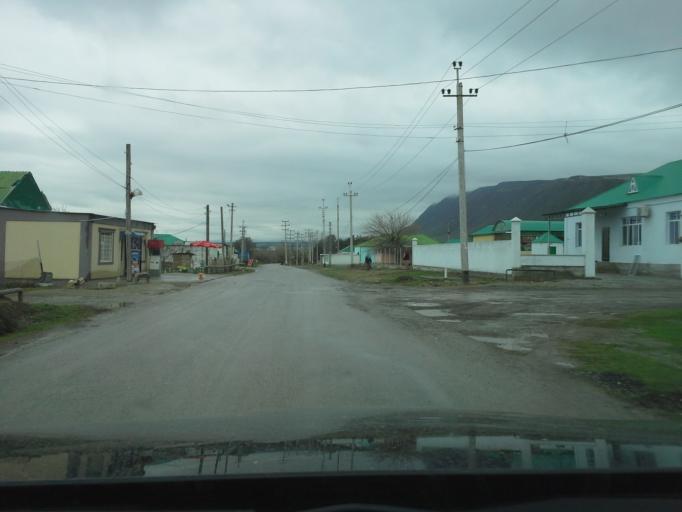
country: TM
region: Ahal
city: Abadan
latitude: 37.9481
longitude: 58.2084
